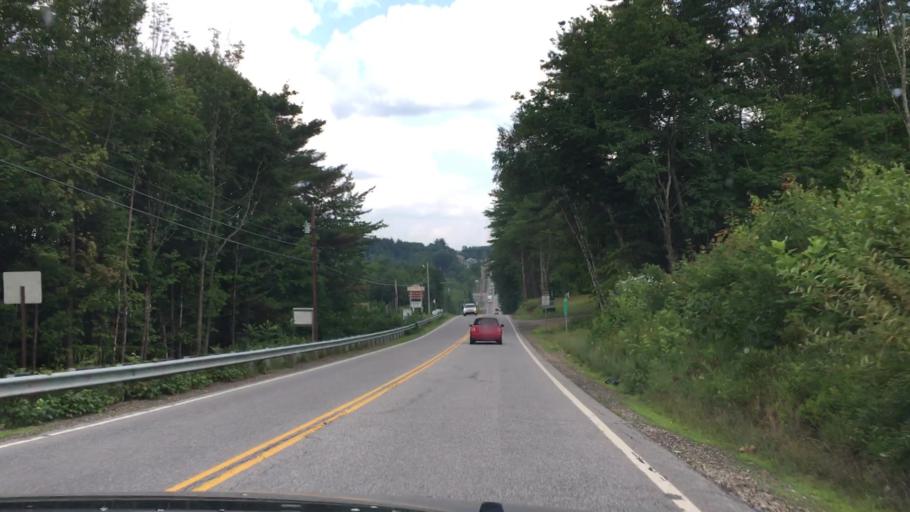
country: US
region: New Hampshire
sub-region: Belknap County
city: Meredith
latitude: 43.6224
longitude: -71.4851
